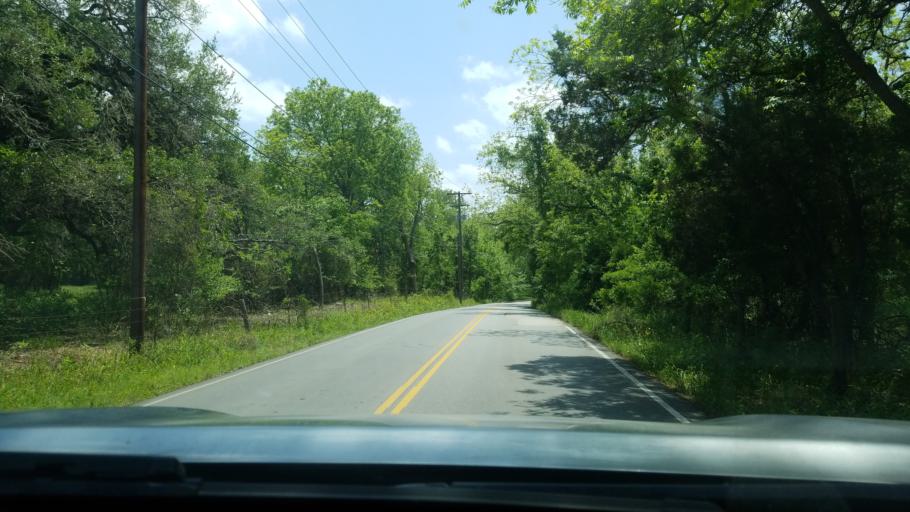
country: US
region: Texas
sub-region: Hays County
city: Woodcreek
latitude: 30.0315
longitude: -98.1221
